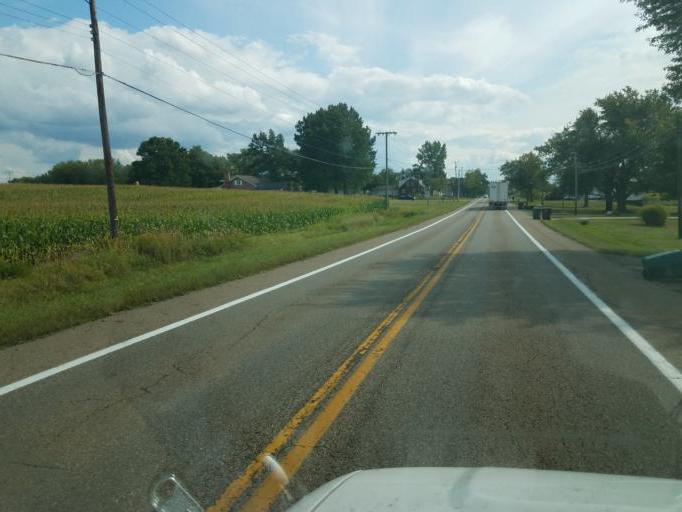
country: US
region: Ohio
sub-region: Stark County
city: Louisville
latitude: 40.8737
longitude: -81.2577
